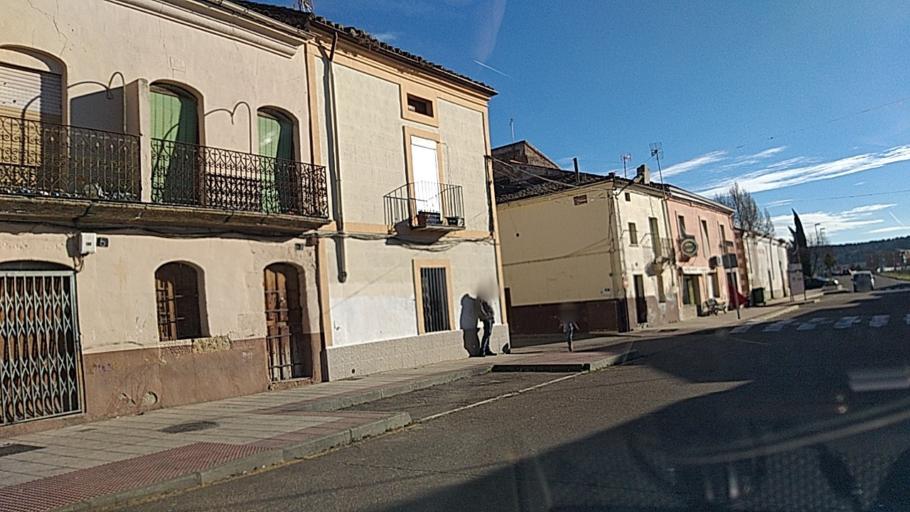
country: ES
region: Castille and Leon
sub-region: Provincia de Salamanca
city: Ciudad Rodrigo
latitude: 40.5940
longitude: -6.5380
